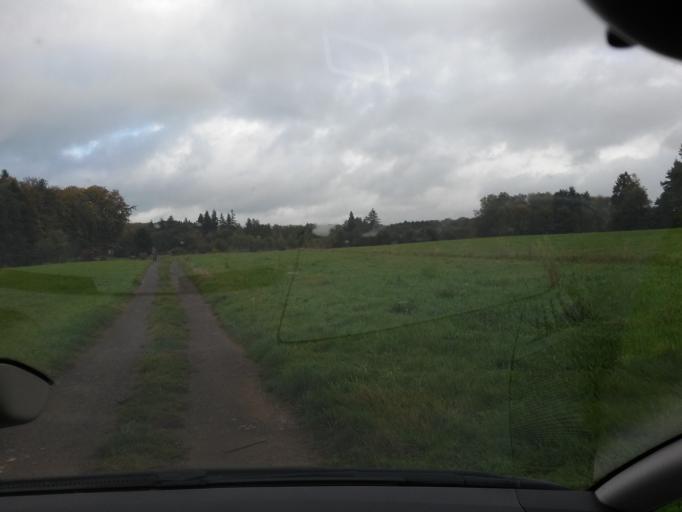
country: BE
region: Wallonia
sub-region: Province du Luxembourg
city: Attert
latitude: 49.7049
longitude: 5.7462
